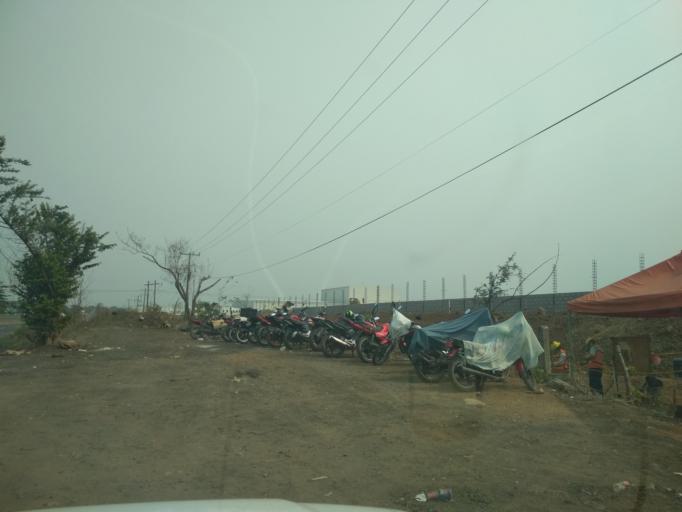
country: MX
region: Veracruz
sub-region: Veracruz
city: Delfino Victoria (Santa Fe)
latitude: 19.1734
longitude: -96.2685
